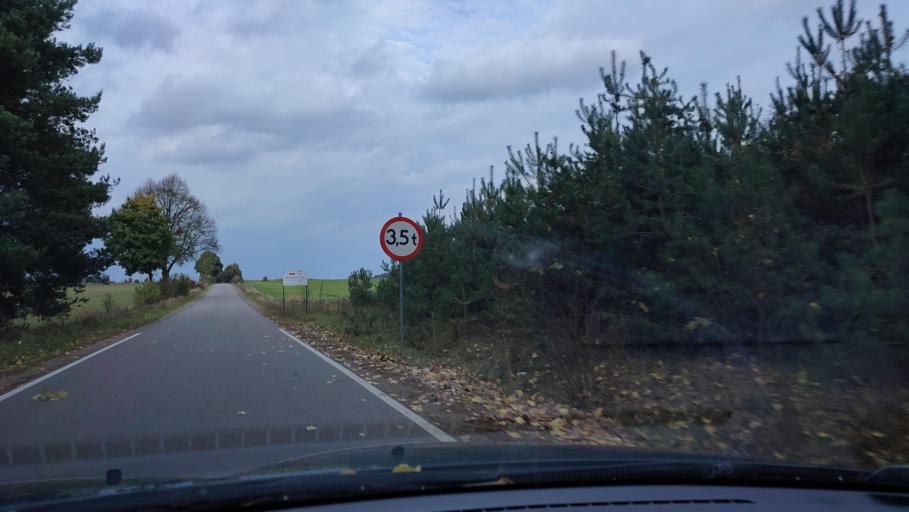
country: PL
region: Masovian Voivodeship
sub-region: Powiat mlawski
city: Mlawa
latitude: 53.1856
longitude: 20.3779
